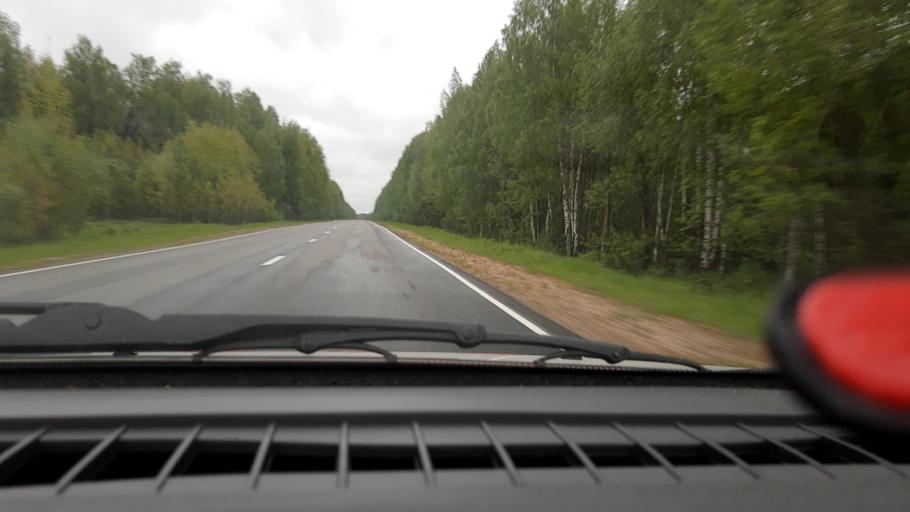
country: RU
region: Nizjnij Novgorod
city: Uren'
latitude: 57.2282
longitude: 45.5357
